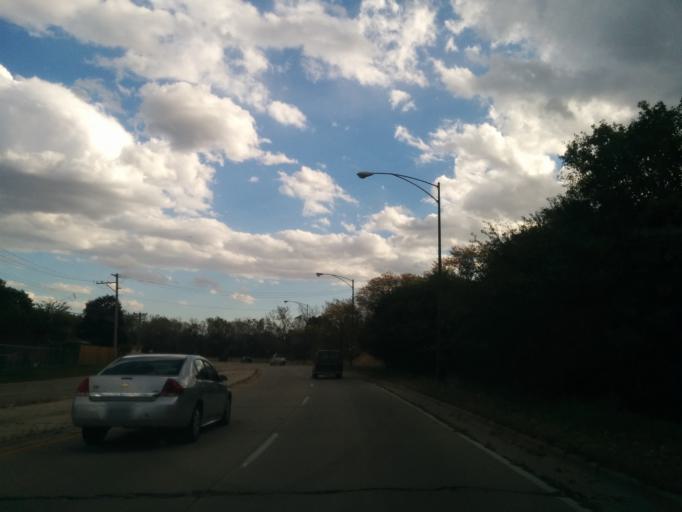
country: US
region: Illinois
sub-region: Cook County
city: Norridge
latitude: 41.9618
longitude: -87.8466
